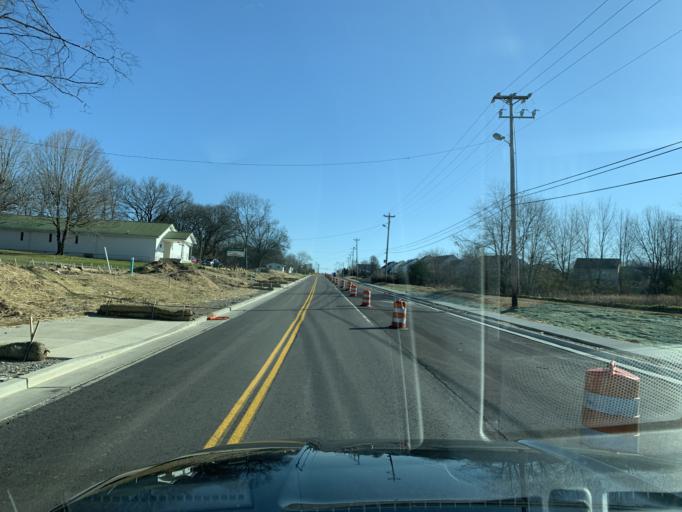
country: US
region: Tennessee
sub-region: Maury County
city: Spring Hill
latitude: 35.7525
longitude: -86.9197
